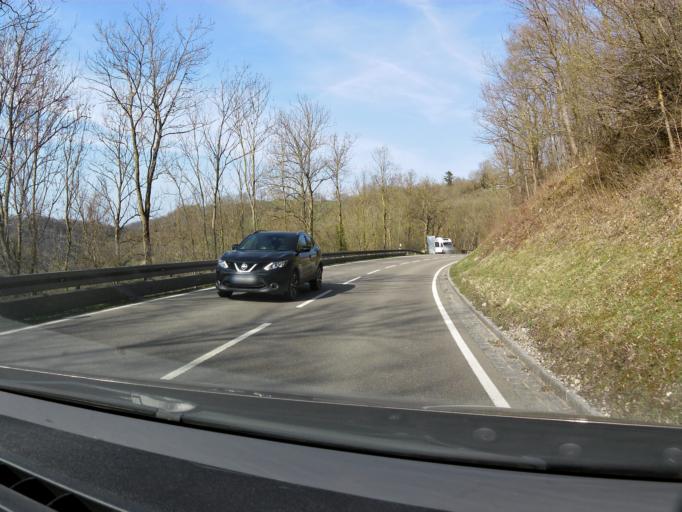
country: DE
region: Bavaria
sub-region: Regierungsbezirk Mittelfranken
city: Rothenburg ob der Tauber
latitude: 49.3852
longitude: 10.1710
